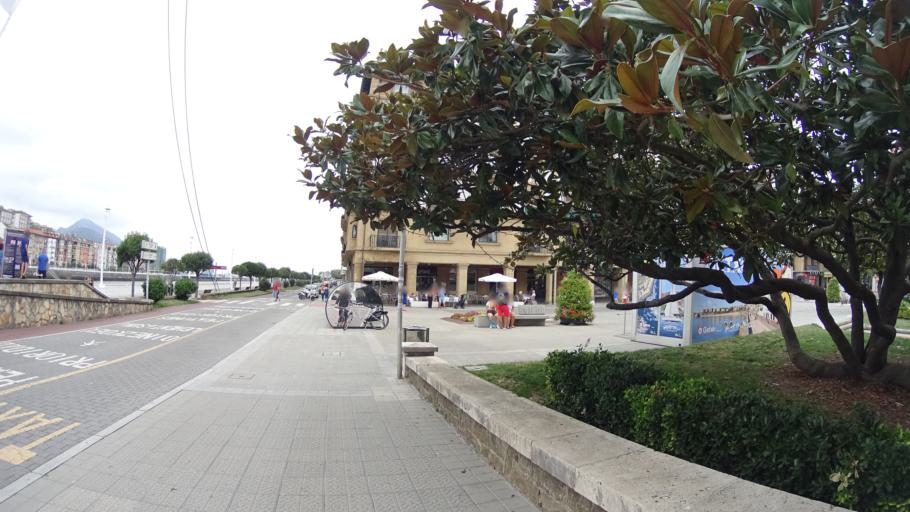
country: ES
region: Basque Country
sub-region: Bizkaia
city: Portugalete
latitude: 43.3238
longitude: -3.0163
